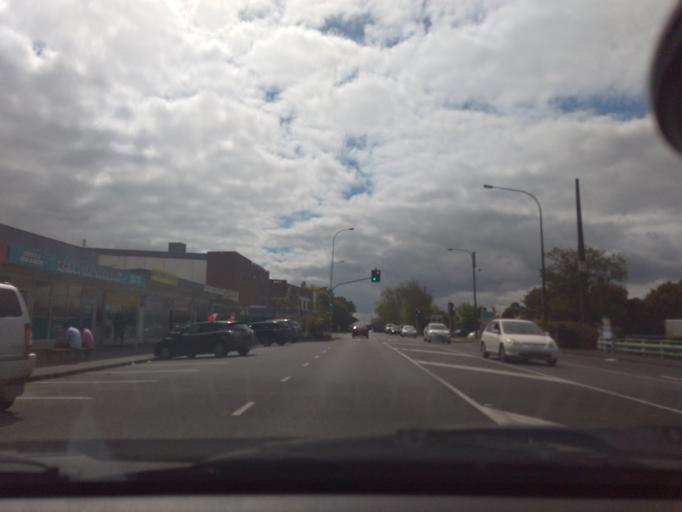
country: NZ
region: Auckland
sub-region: Auckland
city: Rosebank
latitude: -36.8640
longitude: 174.6016
